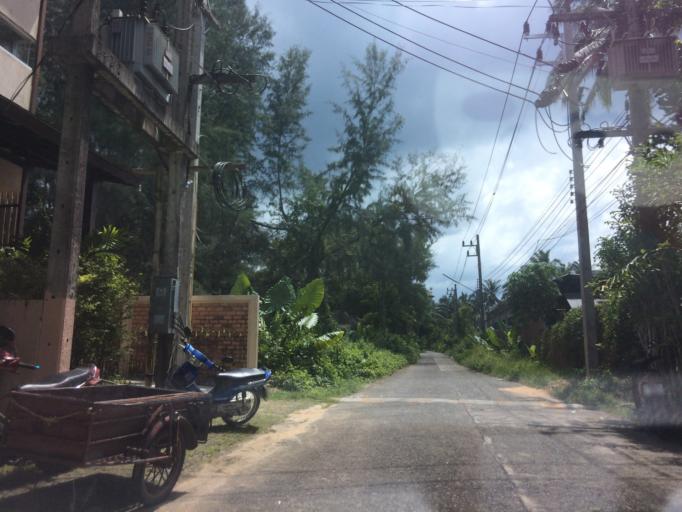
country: TH
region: Phangnga
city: Ban Khao Lak
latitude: 8.6708
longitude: 98.2434
